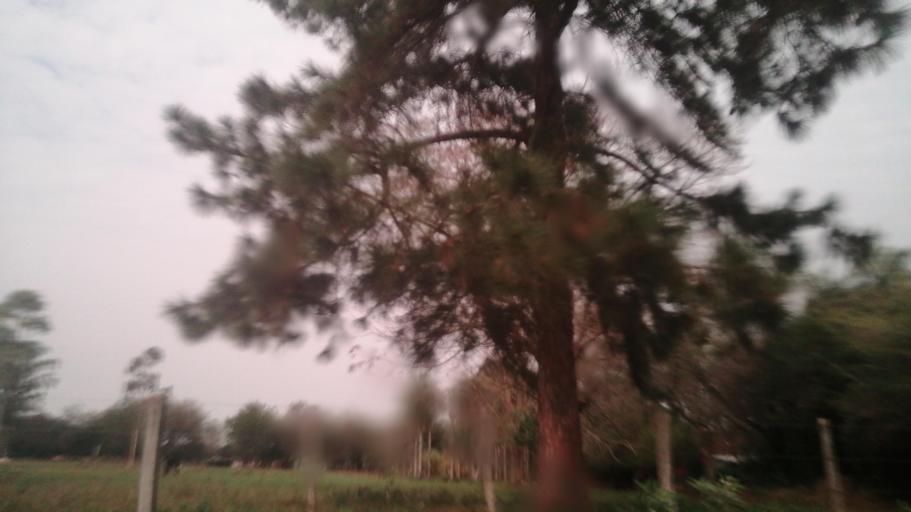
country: PY
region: Misiones
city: San Juan Bautista
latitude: -26.6737
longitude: -57.1493
